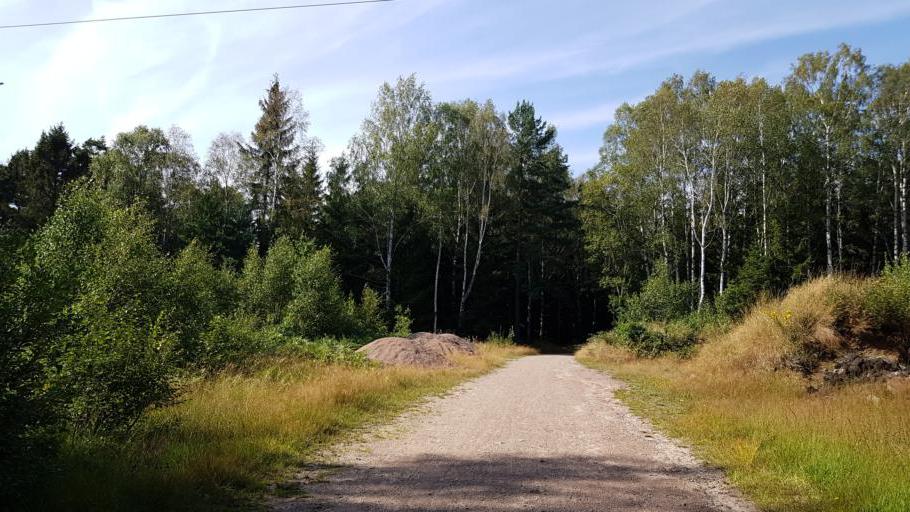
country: SE
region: Vaestra Goetaland
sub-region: Harryda Kommun
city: Molnlycke
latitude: 57.6774
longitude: 12.0702
